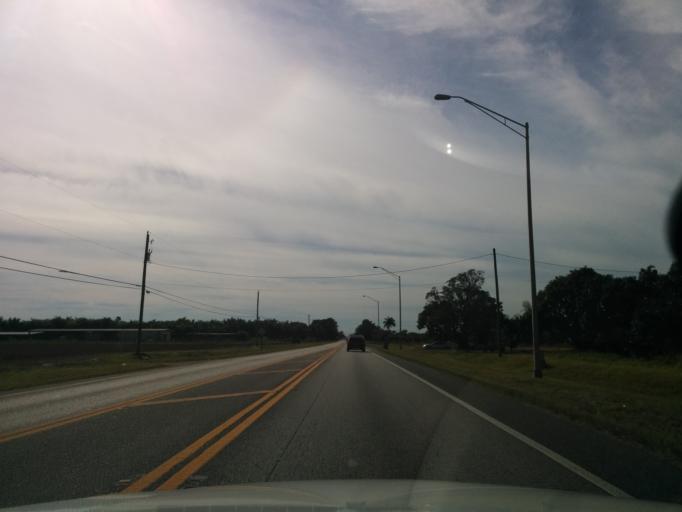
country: US
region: Florida
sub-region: Miami-Dade County
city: Homestead
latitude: 25.5118
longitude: -80.4778
